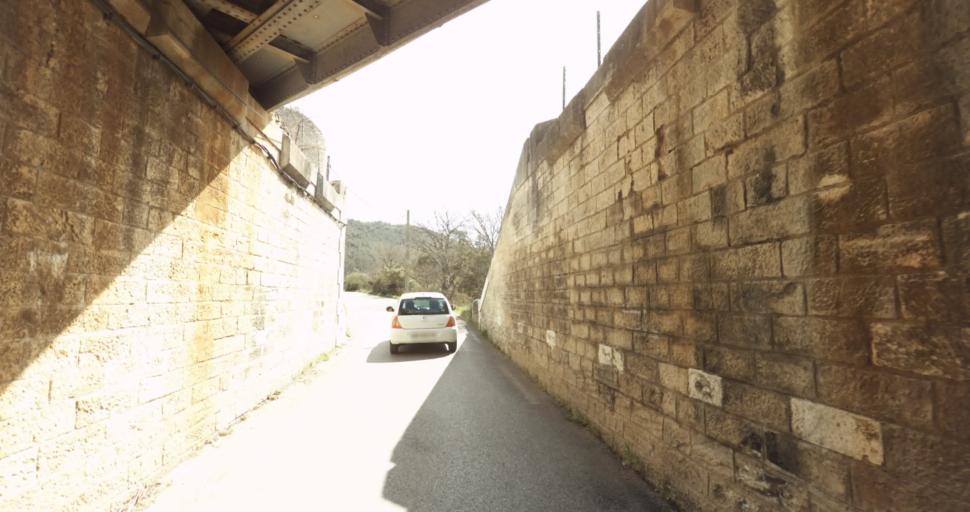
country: FR
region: Provence-Alpes-Cote d'Azur
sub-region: Departement des Bouches-du-Rhone
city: Ventabren
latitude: 43.5167
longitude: 5.3041
